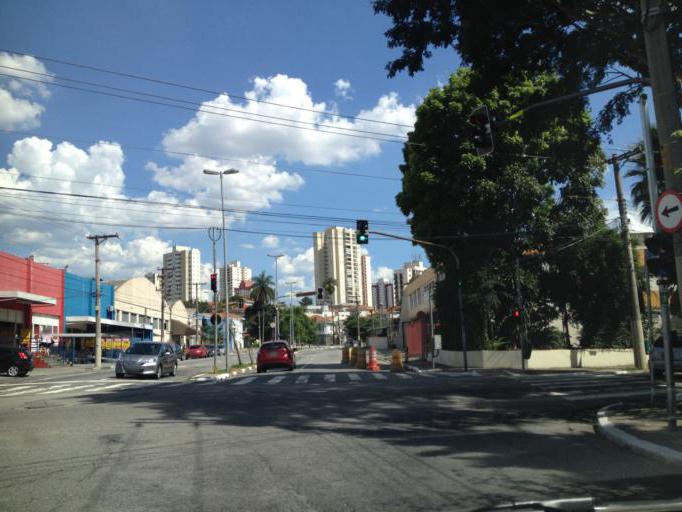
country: BR
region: Sao Paulo
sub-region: Sao Paulo
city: Sao Paulo
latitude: -23.5574
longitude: -46.5857
